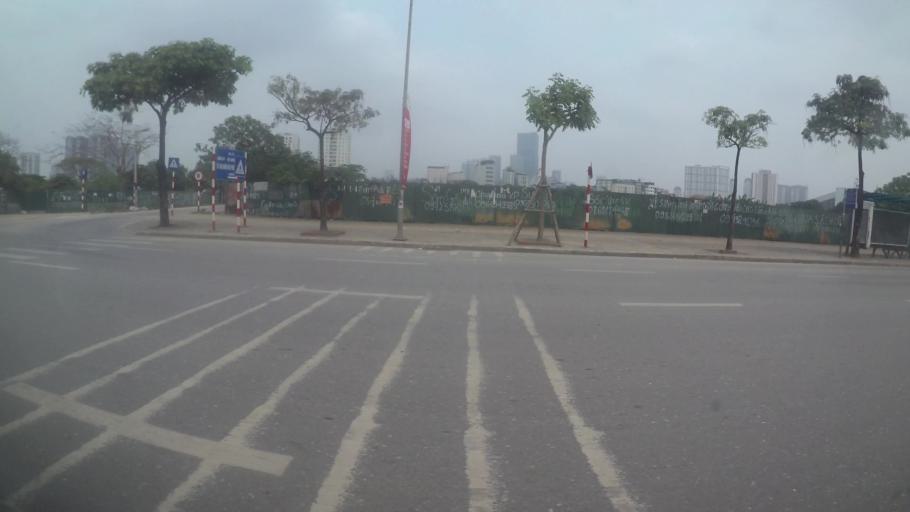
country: VN
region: Ha Noi
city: Cau Dien
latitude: 21.0252
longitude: 105.7676
